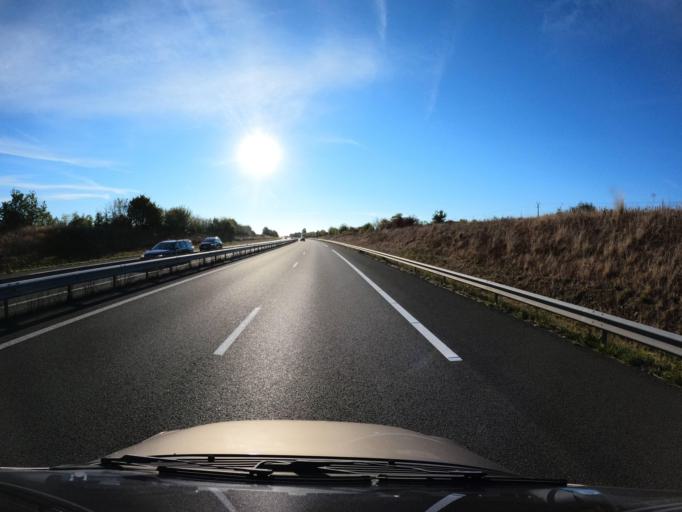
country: FR
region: Pays de la Loire
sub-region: Departement de Maine-et-Loire
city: Chemille-Melay
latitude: 47.2471
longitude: -0.7059
